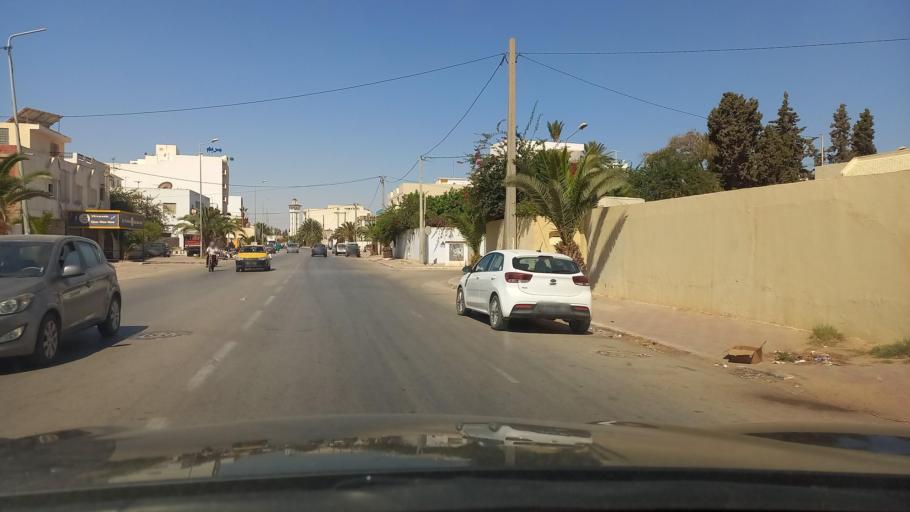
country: TN
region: Safaqis
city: Sfax
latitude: 34.7307
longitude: 10.7354
